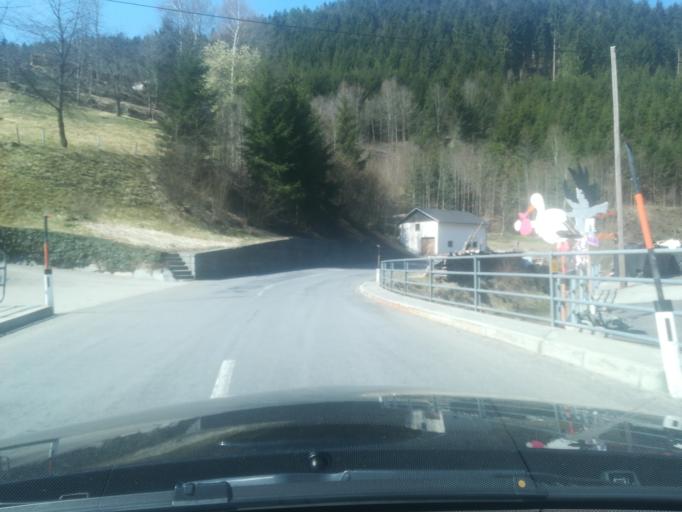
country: AT
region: Upper Austria
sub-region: Politischer Bezirk Perg
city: Sankt Georgen am Walde
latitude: 48.4463
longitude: 14.7825
